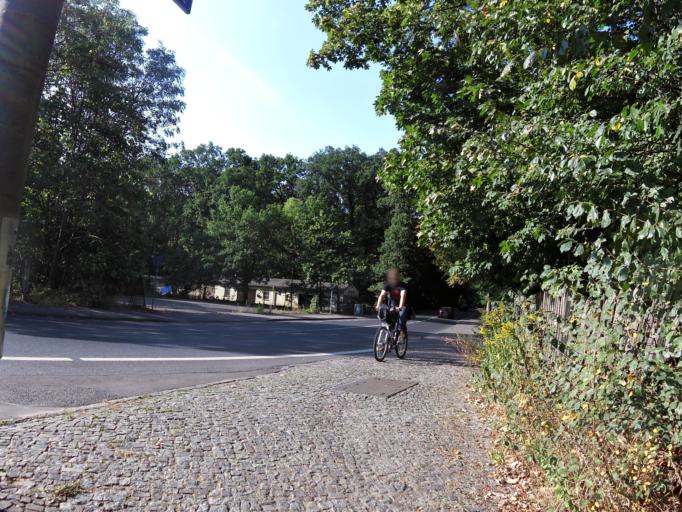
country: DE
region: Saxony
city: Leipzig
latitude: 51.3572
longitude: 12.3154
